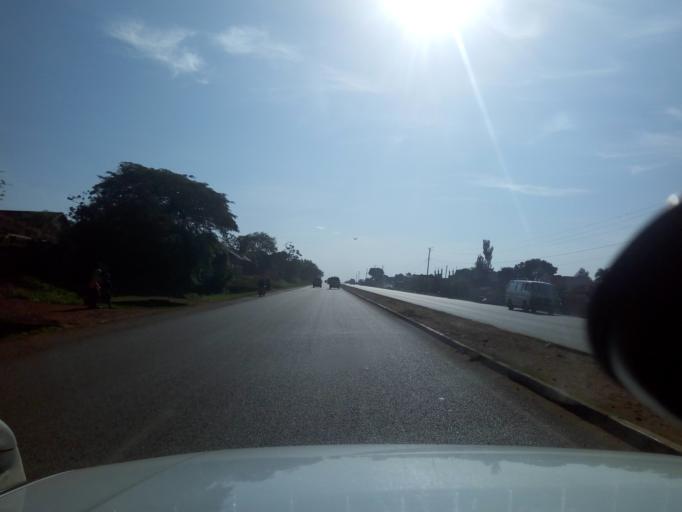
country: UG
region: Eastern Region
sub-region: Jinja District
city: Bugembe
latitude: 0.4689
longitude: 33.2453
